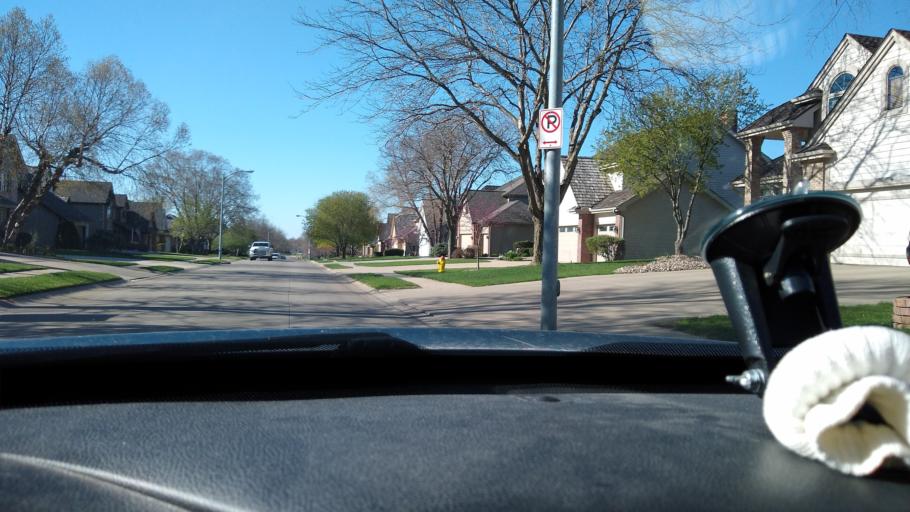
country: US
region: Nebraska
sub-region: Douglas County
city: Ralston
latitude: 41.1964
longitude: -96.0723
